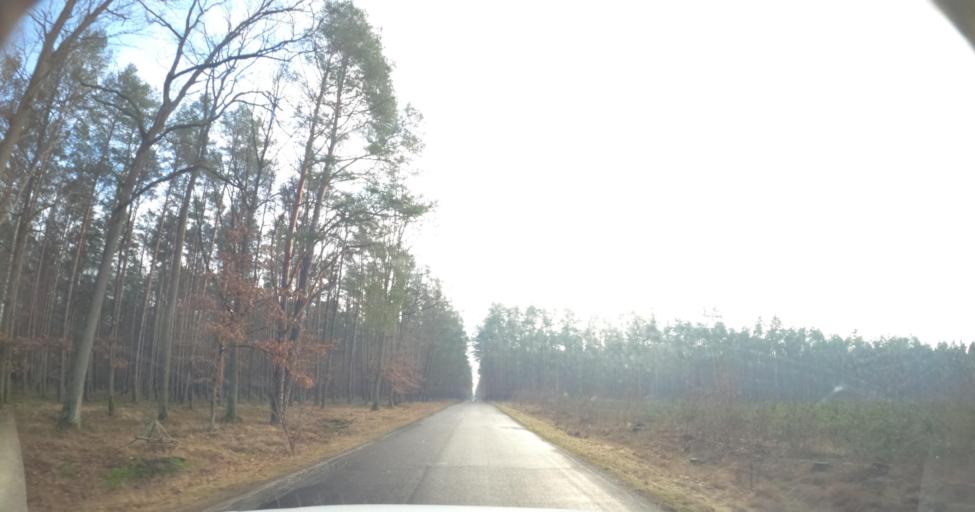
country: PL
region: West Pomeranian Voivodeship
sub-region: Powiat mysliborski
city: Boleszkowice
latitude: 52.6914
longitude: 14.5232
